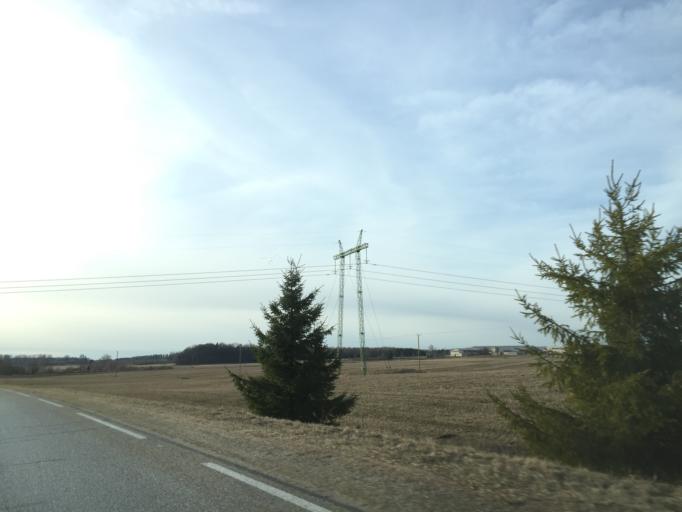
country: LV
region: Krimulda
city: Ragana
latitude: 57.1648
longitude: 24.7797
